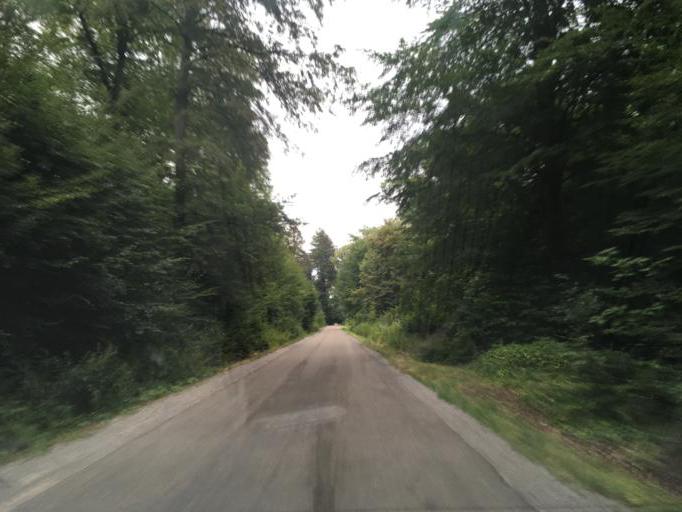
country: DE
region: Baden-Wuerttemberg
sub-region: Tuebingen Region
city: Kusterdingen
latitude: 48.5646
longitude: 9.1192
